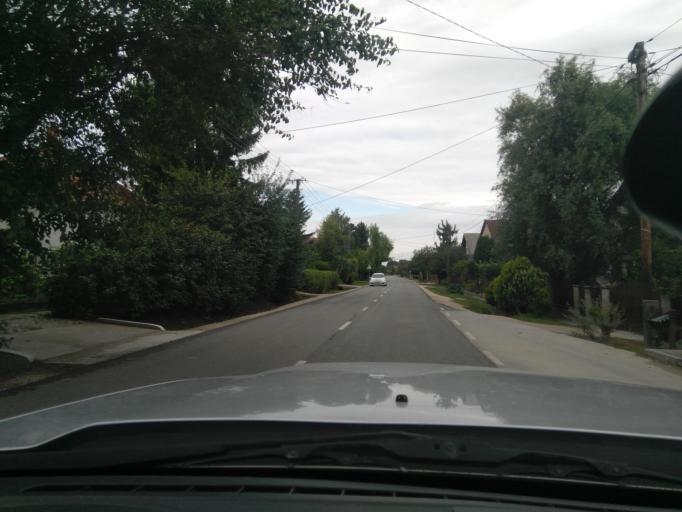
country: HU
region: Fejer
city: Martonvasar
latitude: 47.3450
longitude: 18.7418
